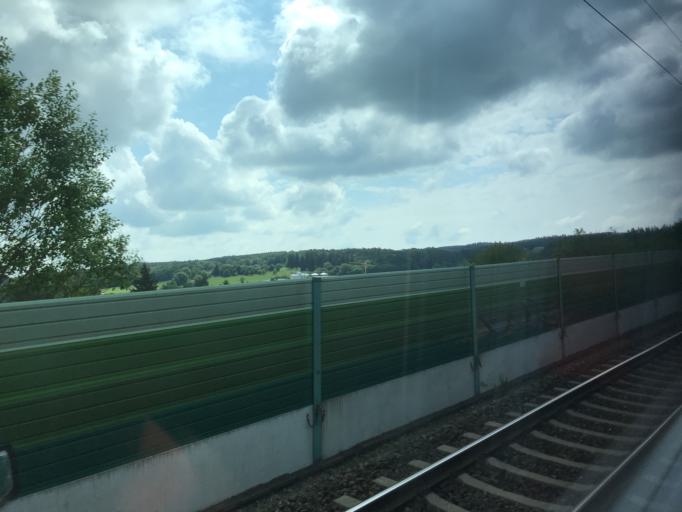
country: DE
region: Baden-Wuerttemberg
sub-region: Tuebingen Region
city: Westerstetten
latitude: 48.5193
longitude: 9.9498
